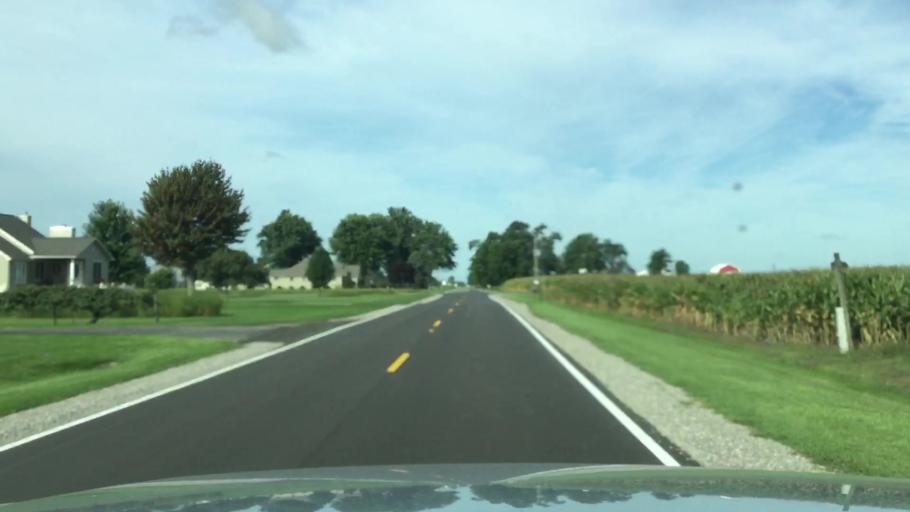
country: US
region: Michigan
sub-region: Genesee County
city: Montrose
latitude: 43.1471
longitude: -83.9474
